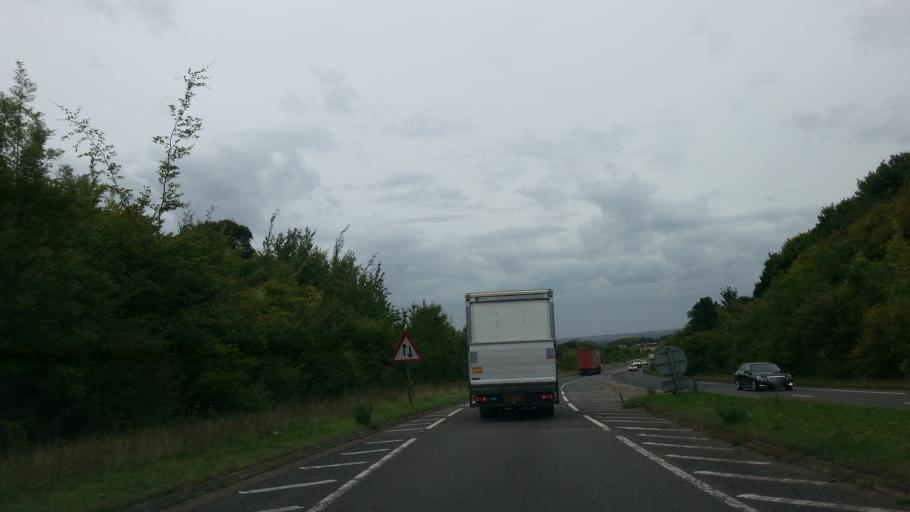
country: GB
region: England
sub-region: Hertfordshire
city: Royston
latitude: 52.0517
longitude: -0.0025
